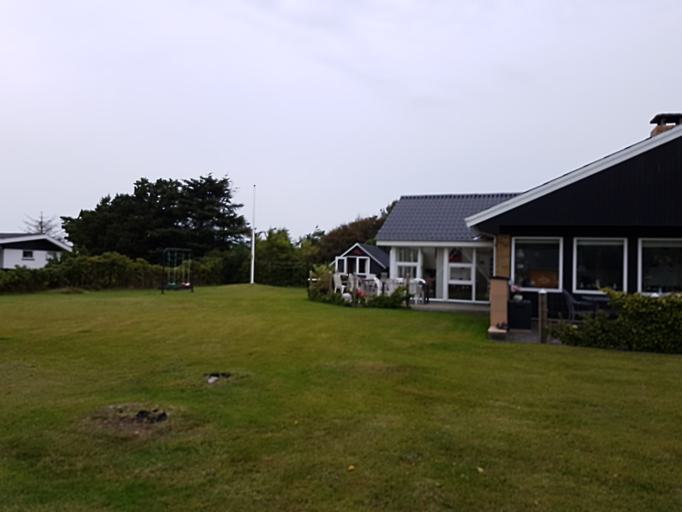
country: DK
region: Central Jutland
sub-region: Ringkobing-Skjern Kommune
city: Hvide Sande
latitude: 55.8500
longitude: 8.2853
